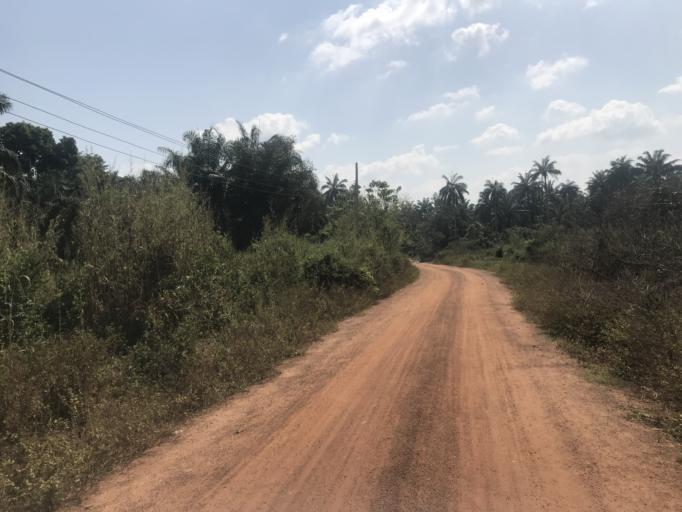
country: NG
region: Osun
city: Iragbiji
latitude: 7.8804
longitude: 4.6998
